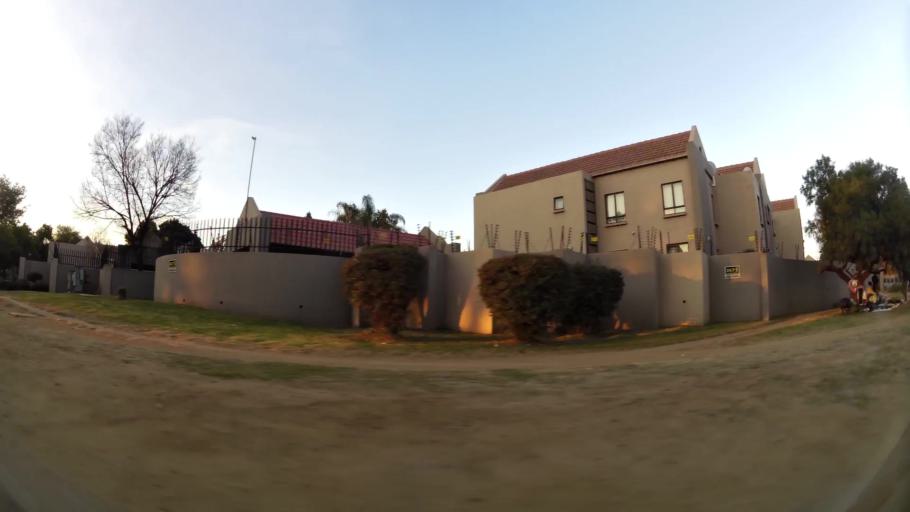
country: ZA
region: Gauteng
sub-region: City of Johannesburg Metropolitan Municipality
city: Midrand
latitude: -26.0566
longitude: 28.0860
